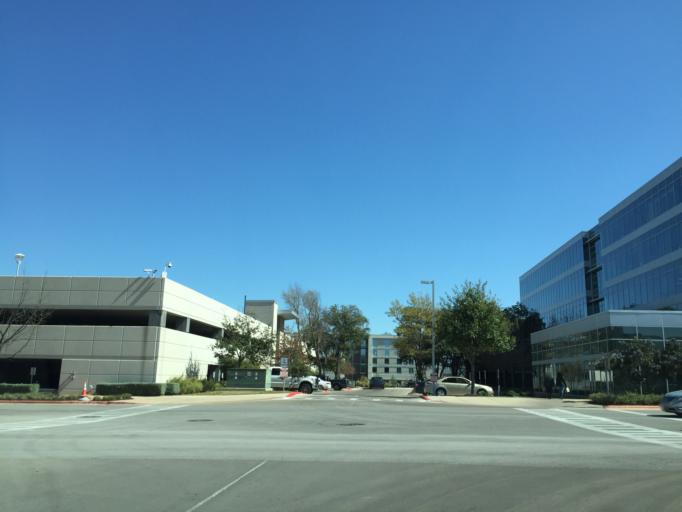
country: US
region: Texas
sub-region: Travis County
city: Wells Branch
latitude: 30.3997
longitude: -97.7206
